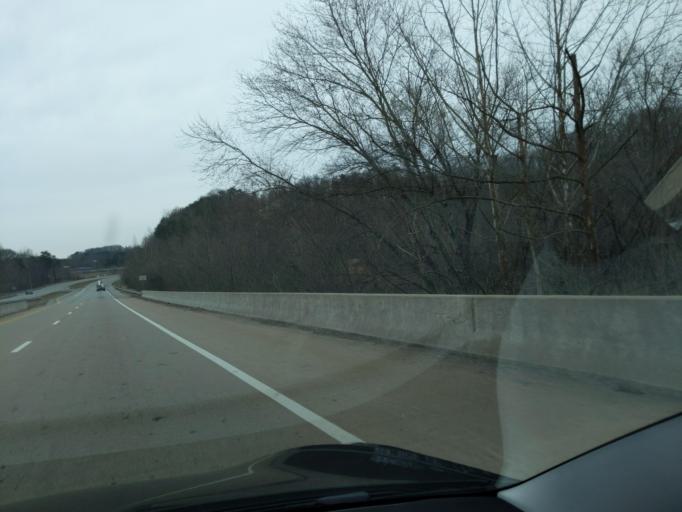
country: US
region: Kentucky
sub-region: Knox County
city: Barbourville
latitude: 36.8466
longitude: -83.7864
